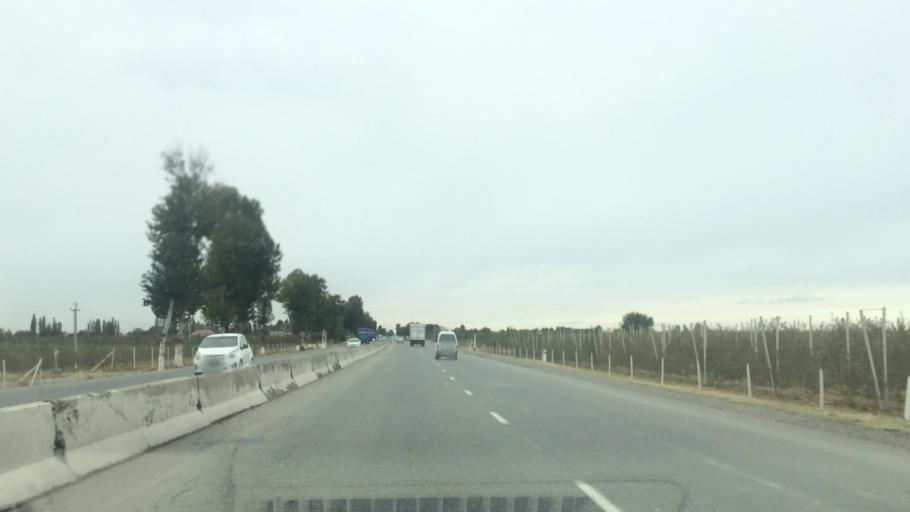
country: UZ
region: Samarqand
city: Jomboy
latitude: 39.7352
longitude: 67.1696
